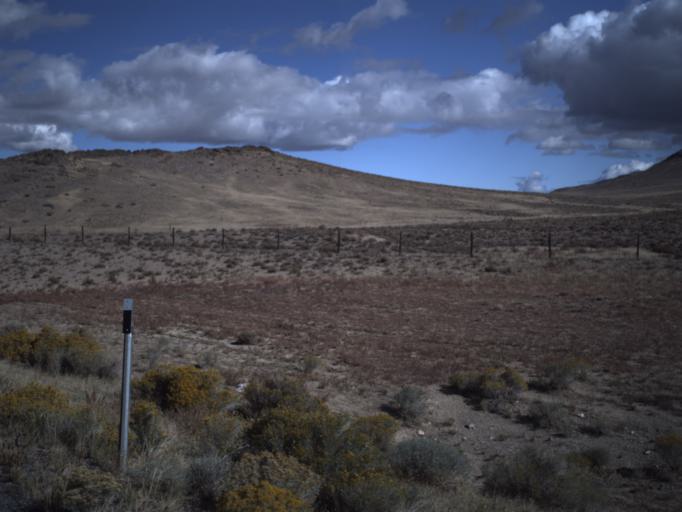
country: US
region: Utah
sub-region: Beaver County
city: Milford
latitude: 38.6258
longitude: -113.8504
